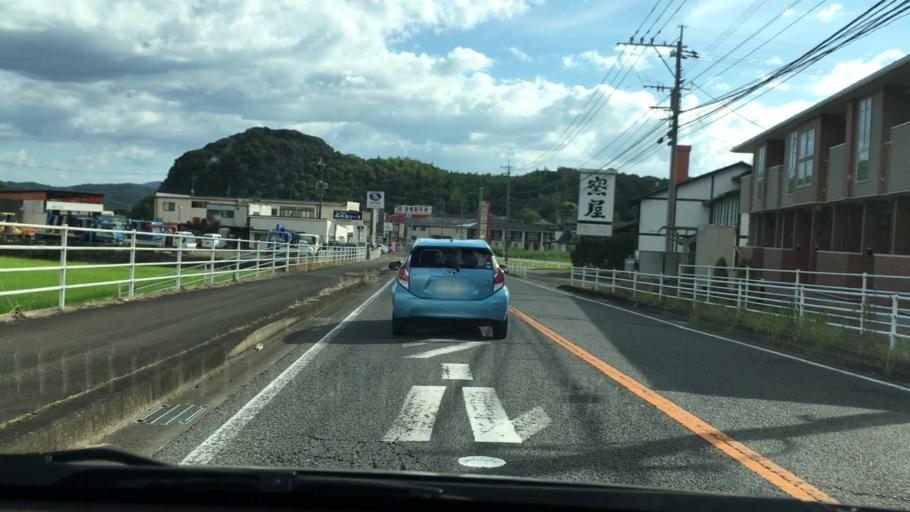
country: JP
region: Nagasaki
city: Sasebo
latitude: 33.1604
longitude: 129.8322
